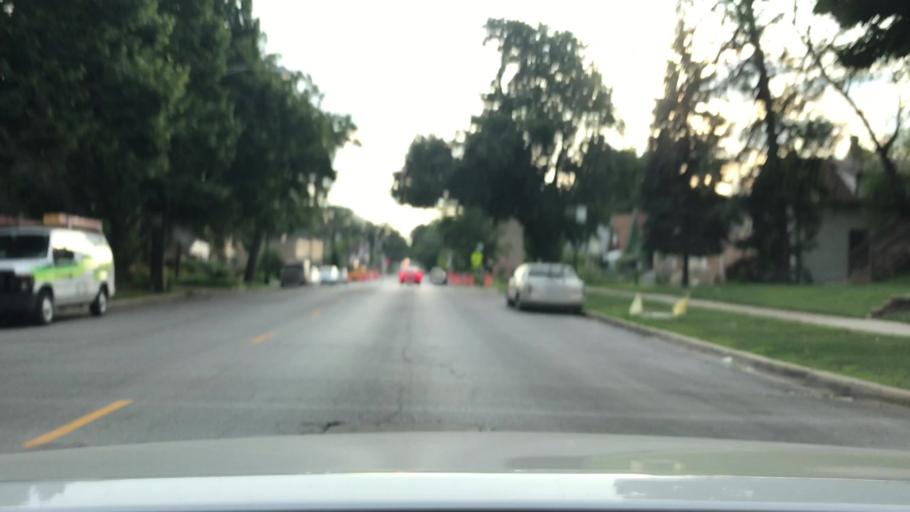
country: US
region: Illinois
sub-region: Cook County
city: Evergreen Park
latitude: 41.7139
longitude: -87.6655
